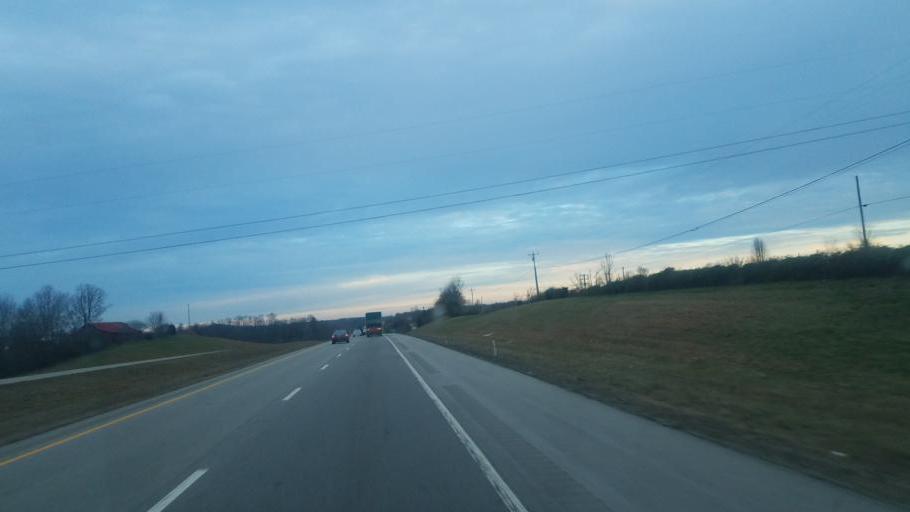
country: US
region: Tennessee
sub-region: Putnam County
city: Cookeville
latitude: 36.0752
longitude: -85.5069
